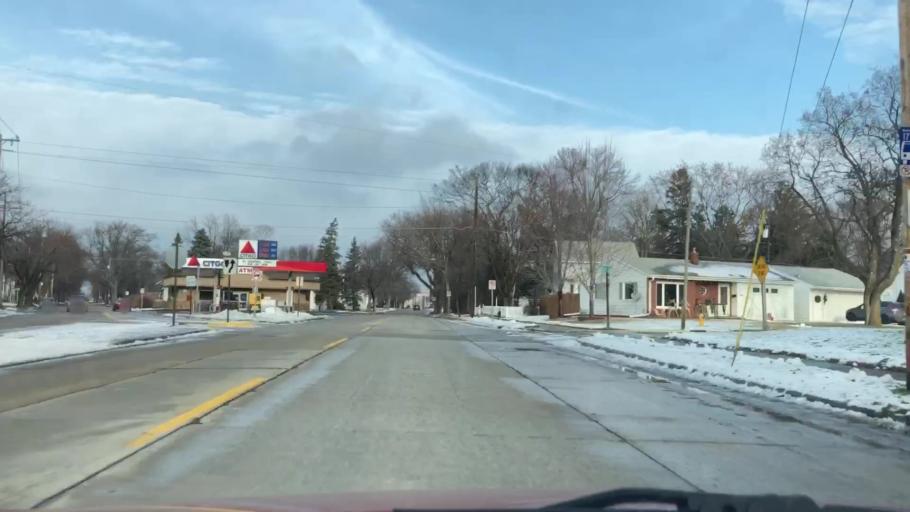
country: US
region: Wisconsin
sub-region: Brown County
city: De Pere
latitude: 44.4373
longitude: -88.0724
